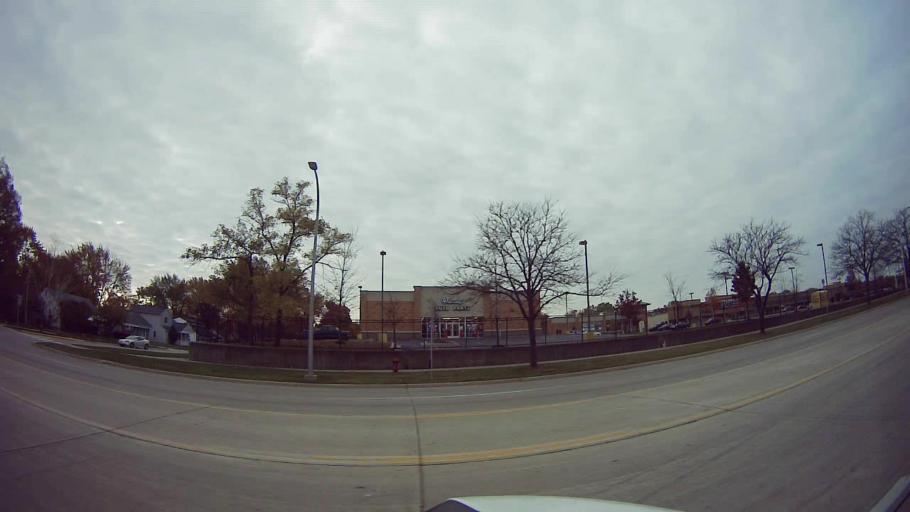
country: US
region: Michigan
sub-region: Oakland County
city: Clawson
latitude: 42.5332
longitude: -83.1607
